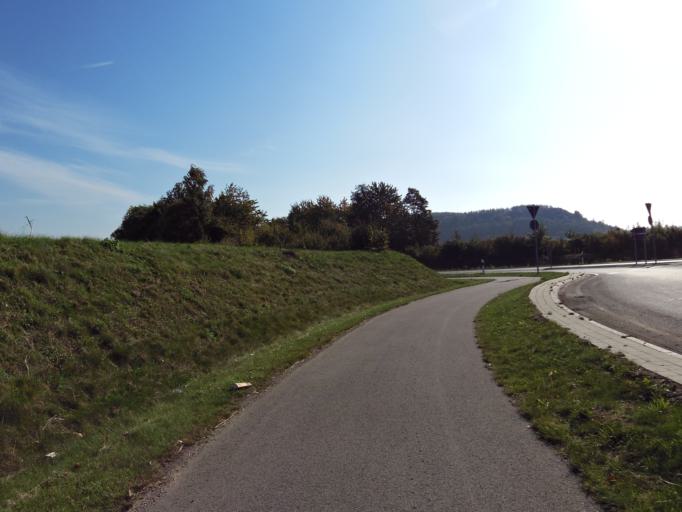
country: DE
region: North Rhine-Westphalia
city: Baesweiler
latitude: 50.9179
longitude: 6.1517
